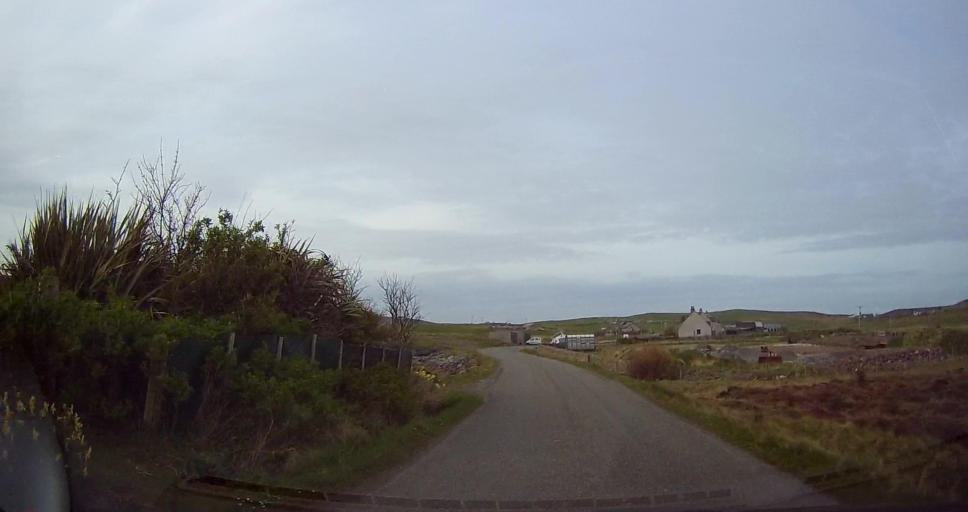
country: GB
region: Scotland
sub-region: Shetland Islands
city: Shetland
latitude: 60.1527
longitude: -1.1156
